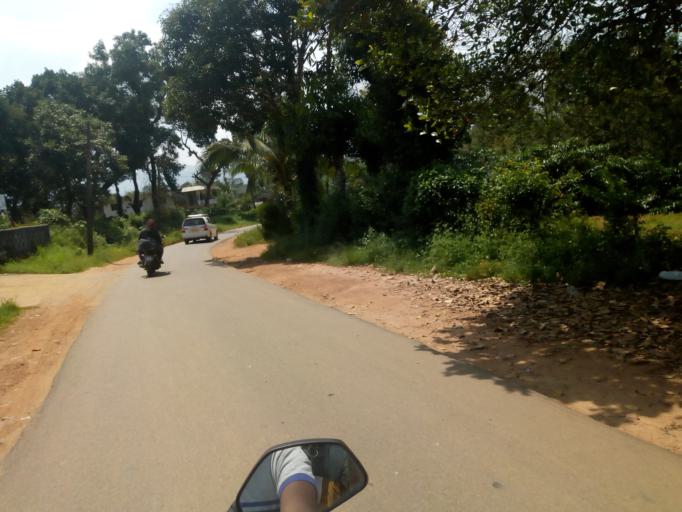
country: IN
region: Karnataka
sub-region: Kodagu
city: Ponnampet
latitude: 12.0322
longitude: 75.9714
